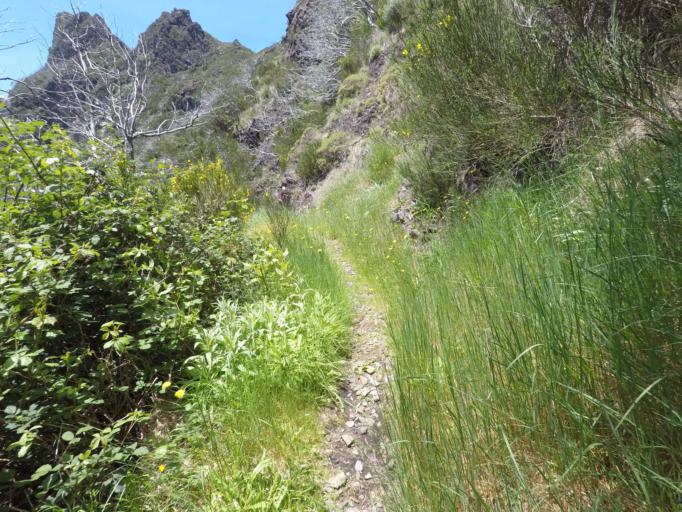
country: PT
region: Madeira
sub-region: Camara de Lobos
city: Curral das Freiras
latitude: 32.7537
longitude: -16.9738
